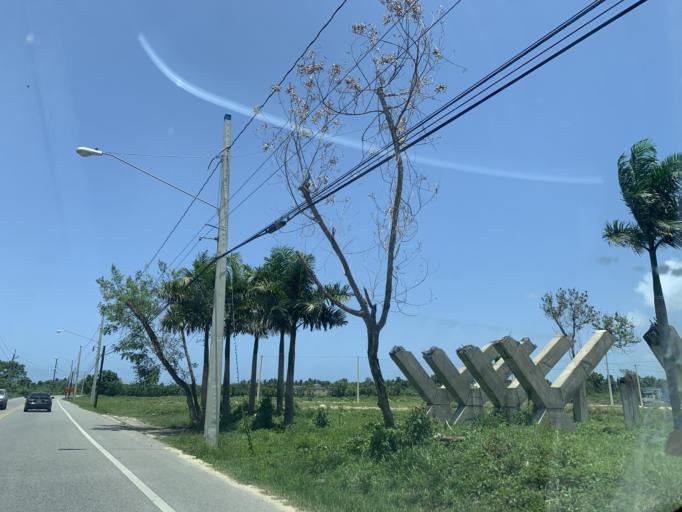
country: DO
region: Puerto Plata
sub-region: Puerto Plata
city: Puerto Plata
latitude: 19.7436
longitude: -70.6004
